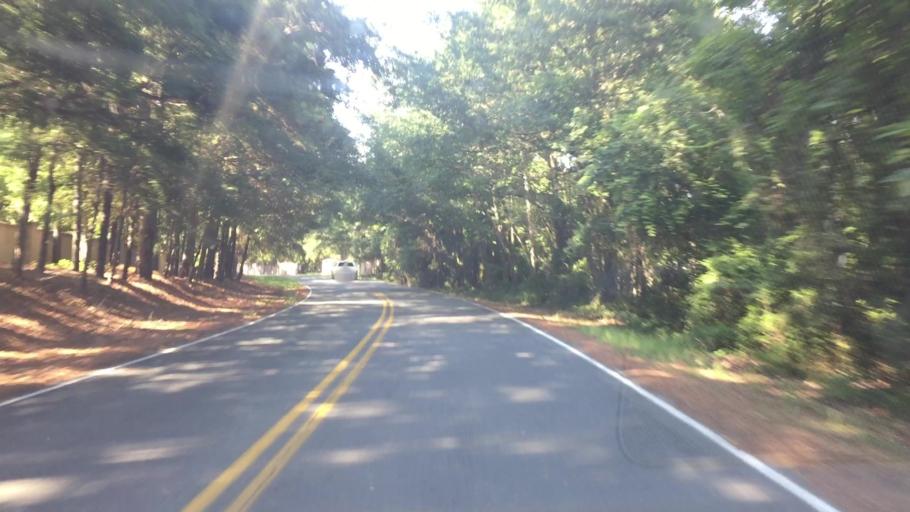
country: US
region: South Carolina
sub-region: Horry County
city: Myrtle Beach
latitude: 33.7535
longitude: -78.8060
